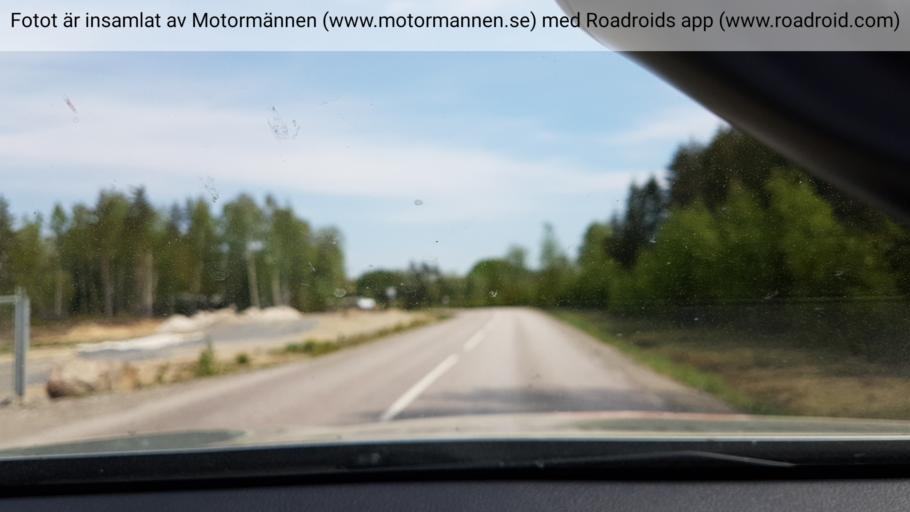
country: SE
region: Stockholm
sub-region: Nynashamns Kommun
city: Osmo
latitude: 59.0456
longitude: 17.8486
